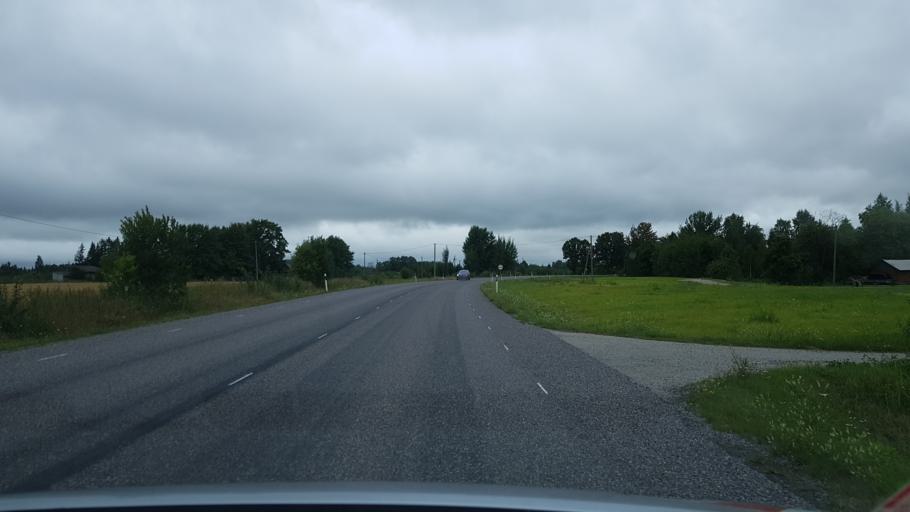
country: EE
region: Polvamaa
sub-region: Polva linn
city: Polva
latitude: 57.9572
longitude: 27.0474
